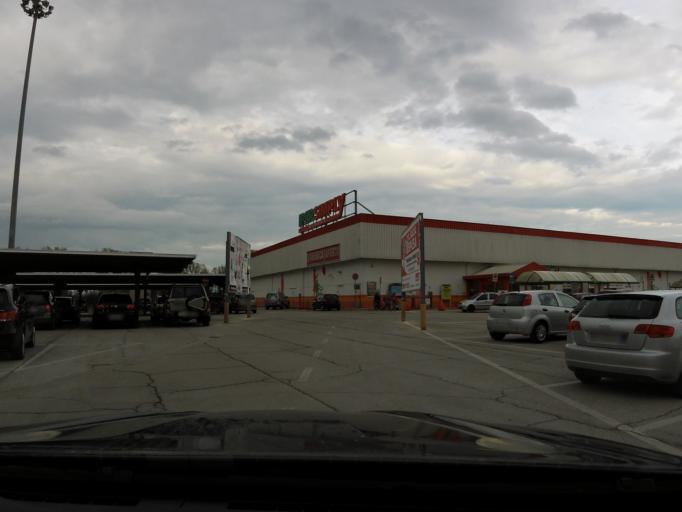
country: IT
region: The Marches
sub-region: Provincia di Ancona
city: Villa Musone
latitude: 43.4550
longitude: 13.5970
